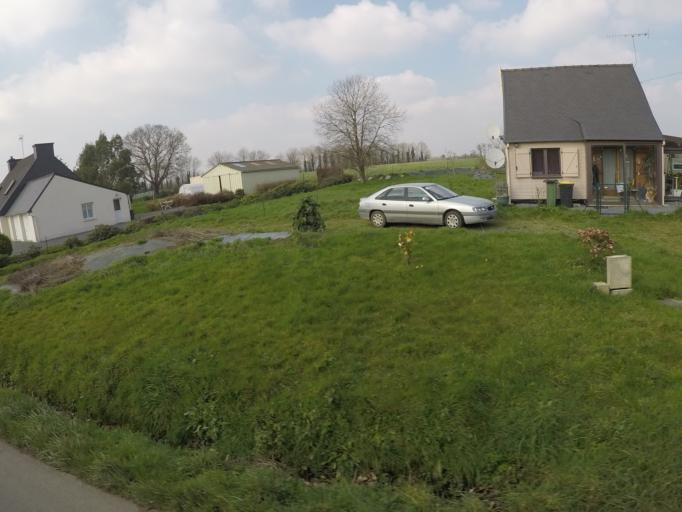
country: FR
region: Brittany
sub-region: Departement des Cotes-d'Armor
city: Goudelin
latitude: 48.6150
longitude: -3.0434
